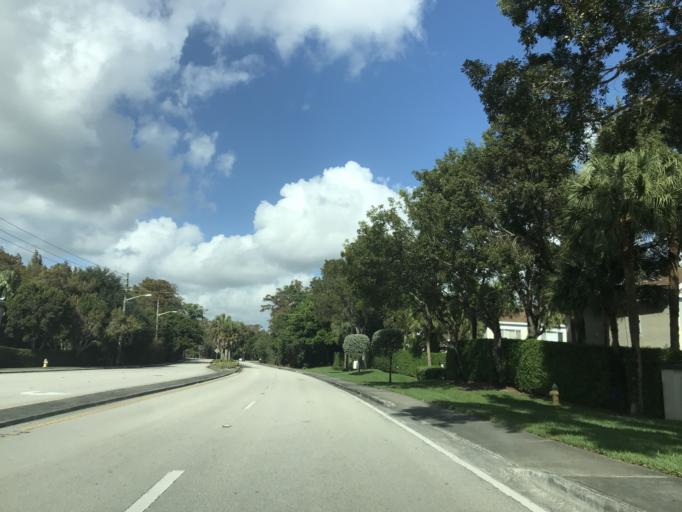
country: US
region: Florida
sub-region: Broward County
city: Margate
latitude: 26.2683
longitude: -80.1991
